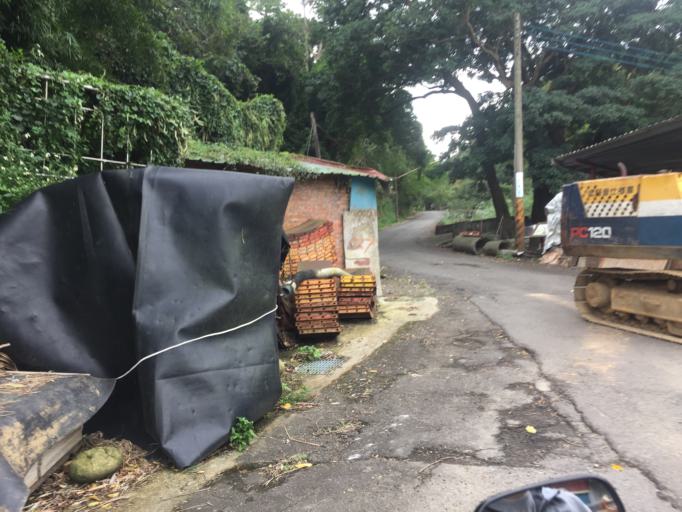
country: TW
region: Taiwan
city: Daxi
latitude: 24.7904
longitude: 121.1650
